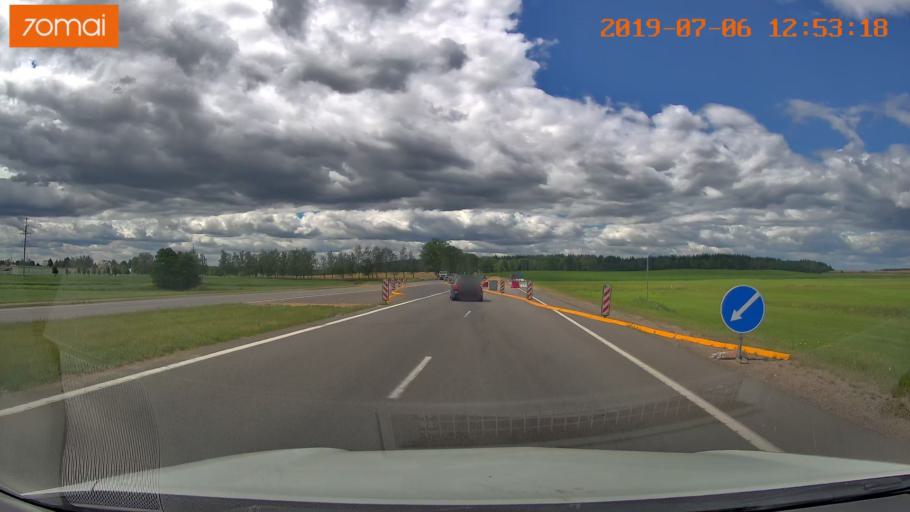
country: BY
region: Minsk
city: Dzyarzhynsk
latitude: 53.7041
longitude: 27.2048
